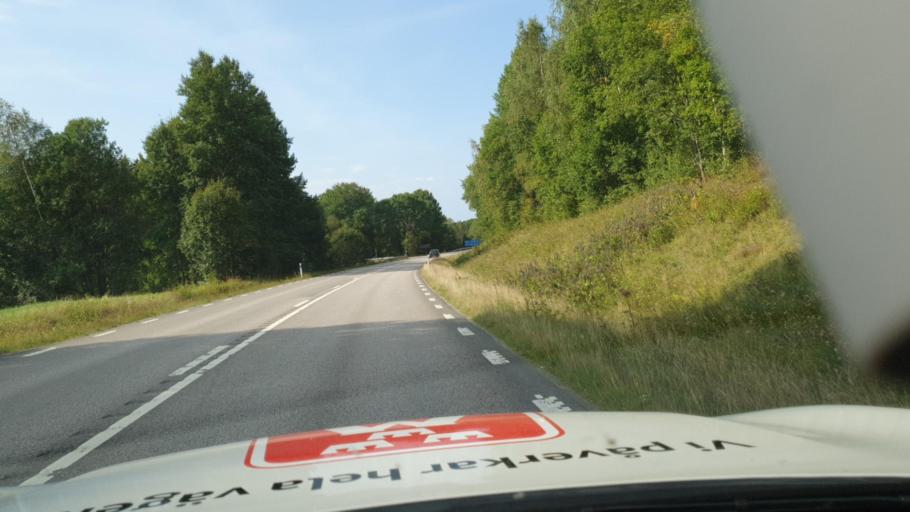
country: SE
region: Vaestra Goetaland
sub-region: Dals-Ed Kommun
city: Ed
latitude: 58.8799
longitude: 11.8996
